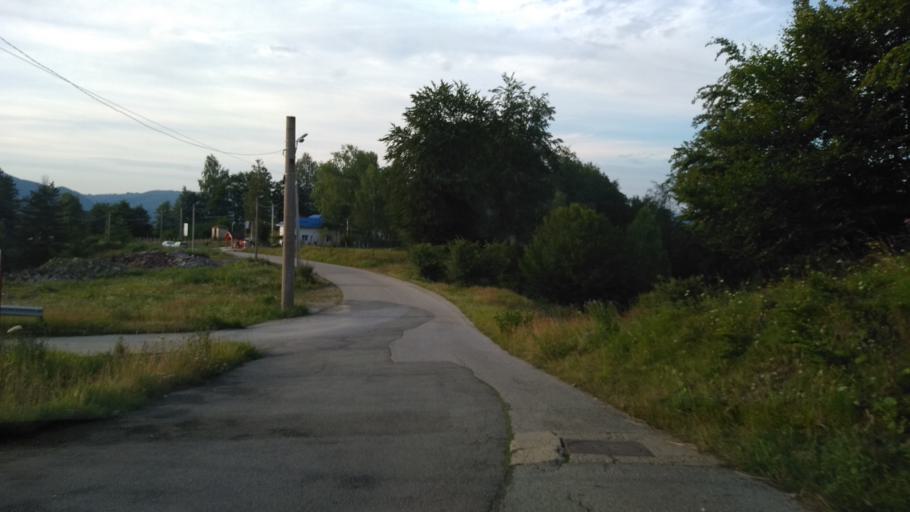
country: RO
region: Hunedoara
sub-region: Municipiul  Vulcan
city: Jiu-Paroseni
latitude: 45.3539
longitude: 23.2909
